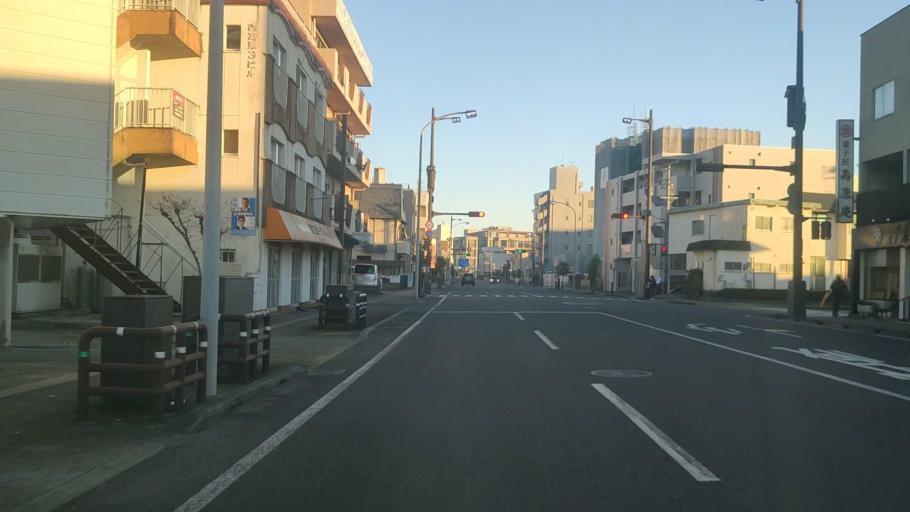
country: JP
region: Miyazaki
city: Miyazaki-shi
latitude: 31.9110
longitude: 131.4161
